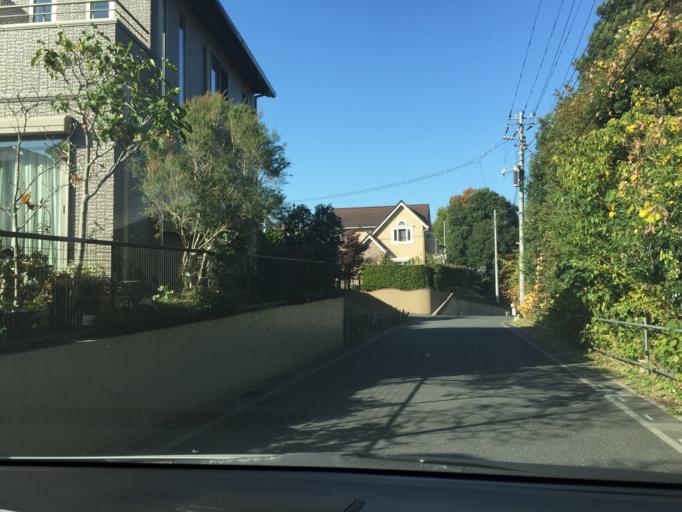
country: JP
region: Saitama
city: Koshigaya
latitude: 35.8896
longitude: 139.7298
